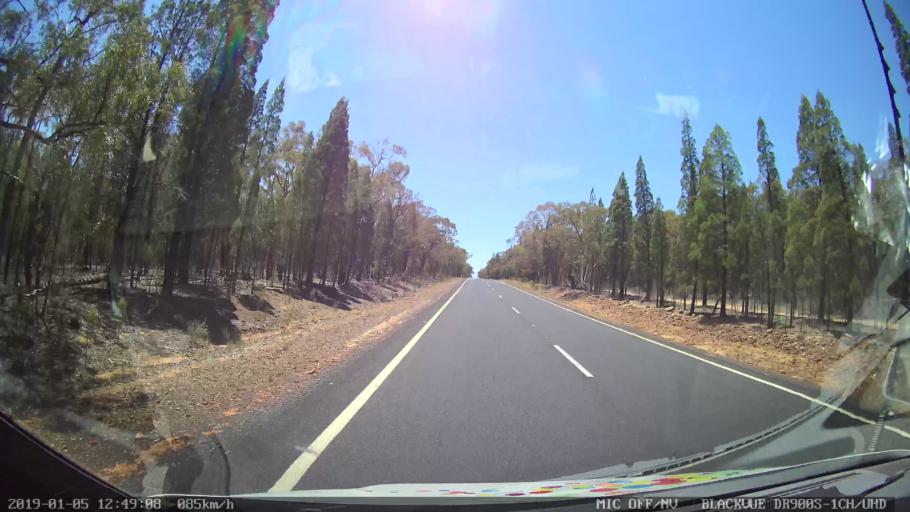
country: AU
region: New South Wales
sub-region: Warrumbungle Shire
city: Coonabarabran
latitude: -31.1178
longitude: 149.6025
